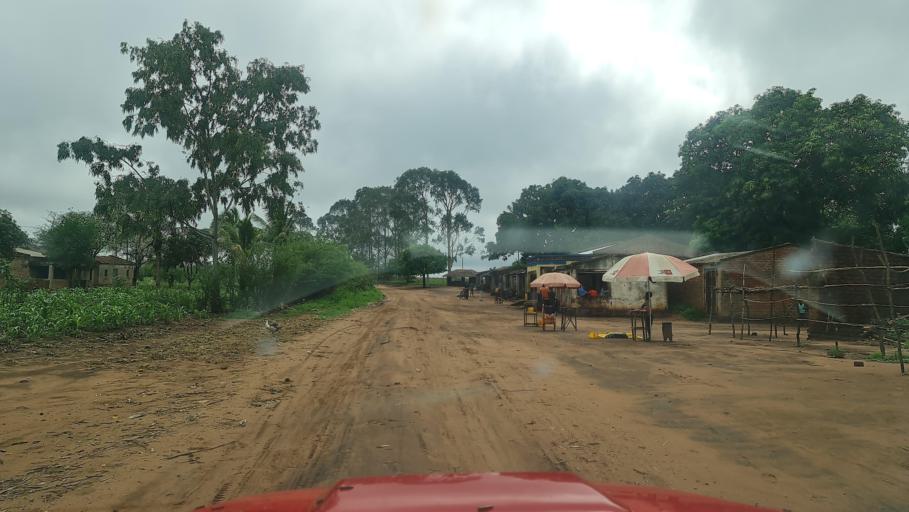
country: MW
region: Southern Region
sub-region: Nsanje District
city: Nsanje
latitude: -17.2031
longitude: 35.6968
